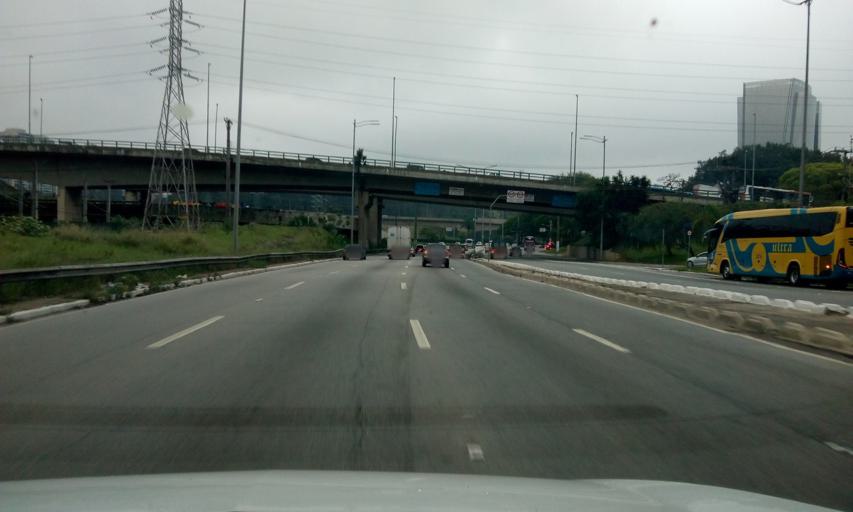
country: BR
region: Sao Paulo
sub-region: Taboao Da Serra
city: Taboao da Serra
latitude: -23.6458
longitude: -46.7256
